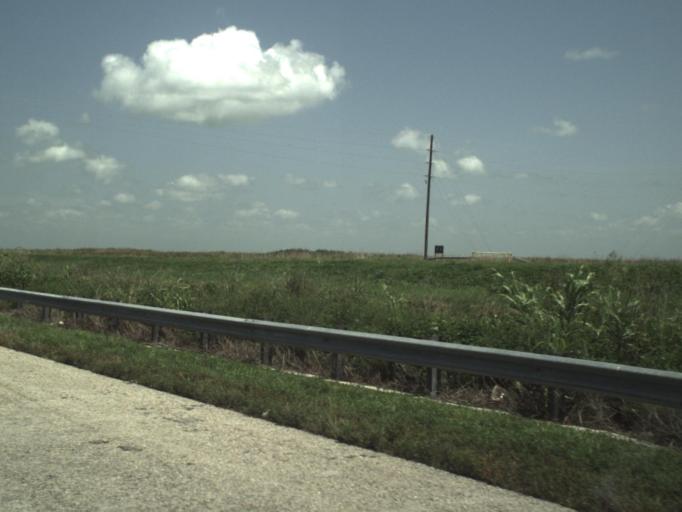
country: US
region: Florida
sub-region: Palm Beach County
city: Belle Glade Camp
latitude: 26.4051
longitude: -80.5919
